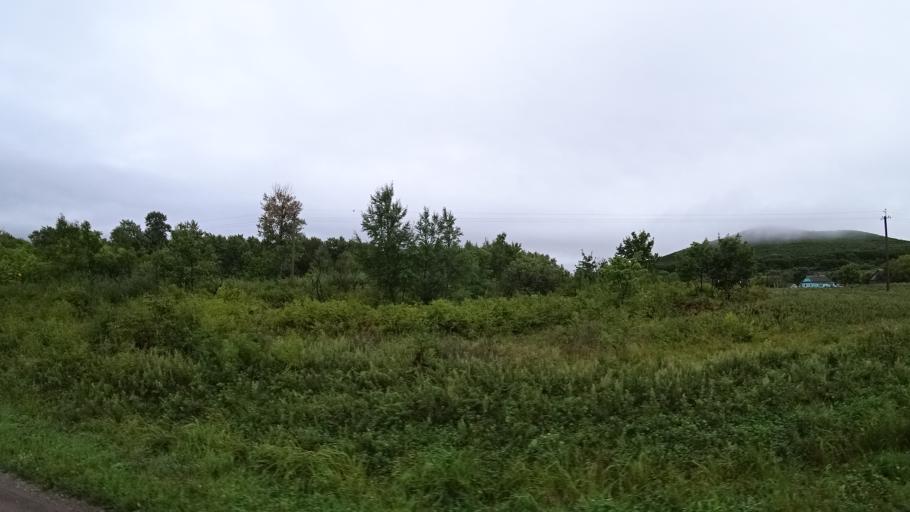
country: RU
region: Primorskiy
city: Monastyrishche
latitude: 44.2715
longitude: 132.4218
